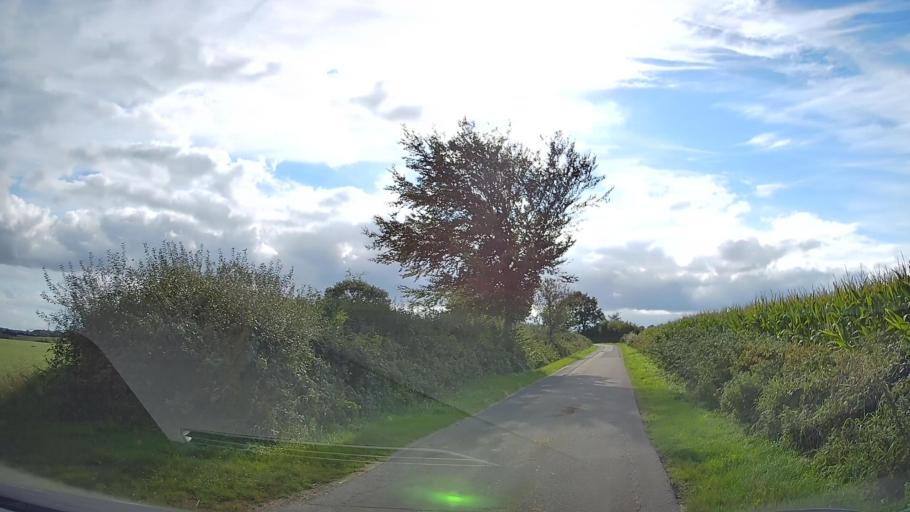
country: DE
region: Schleswig-Holstein
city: Ringsberg
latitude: 54.8189
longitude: 9.5934
